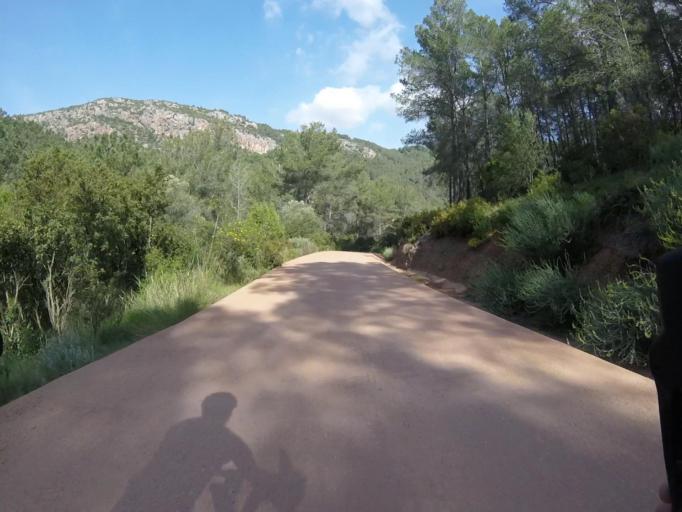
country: ES
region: Valencia
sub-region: Provincia de Castello
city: Cabanes
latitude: 40.1014
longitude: 0.0369
